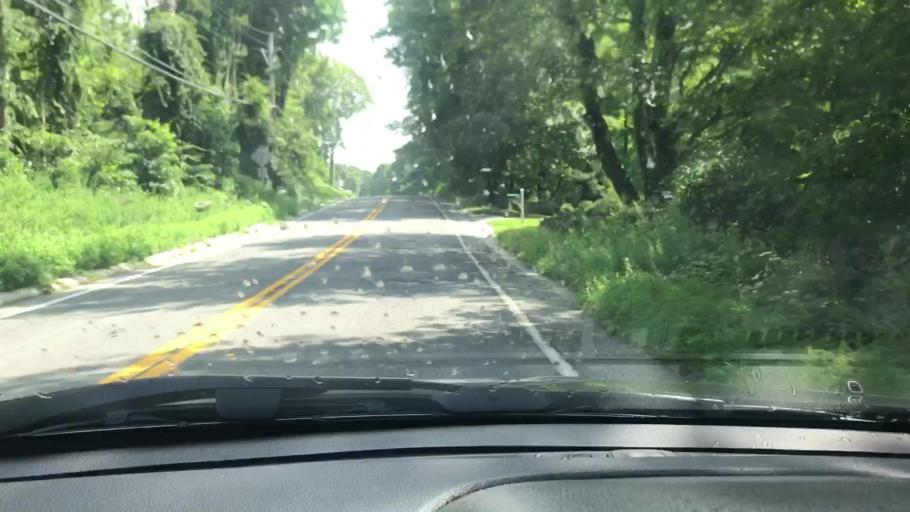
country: US
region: New York
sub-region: Westchester County
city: Bedford
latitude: 41.1841
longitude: -73.6152
